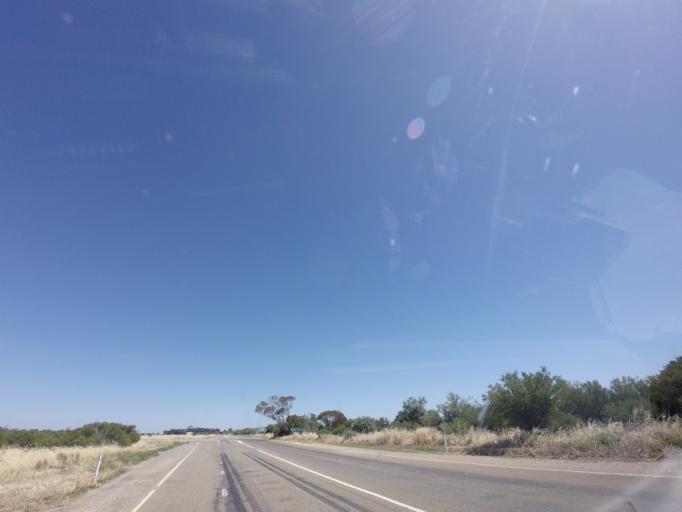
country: AU
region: South Australia
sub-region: Peterborough
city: Peterborough
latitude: -32.8159
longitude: 138.6866
